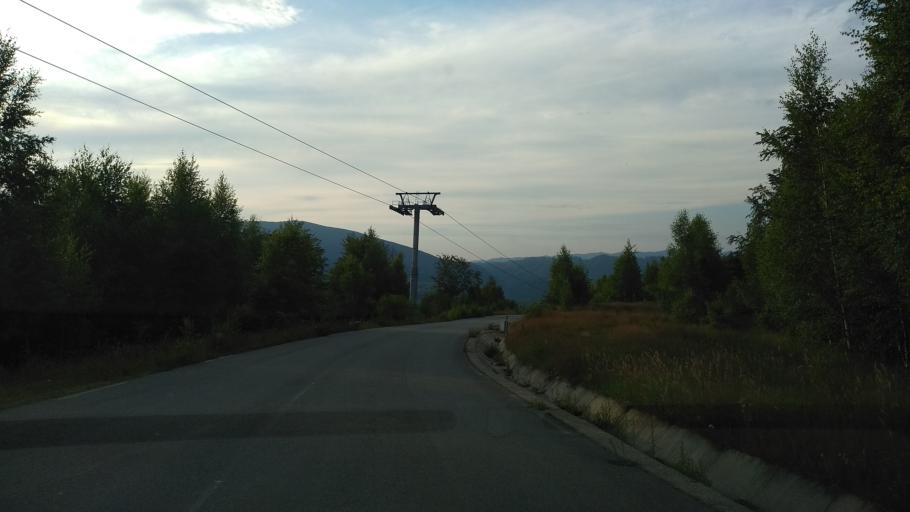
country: RO
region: Hunedoara
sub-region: Municipiul  Vulcan
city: Jiu-Paroseni
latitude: 45.3487
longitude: 23.2904
